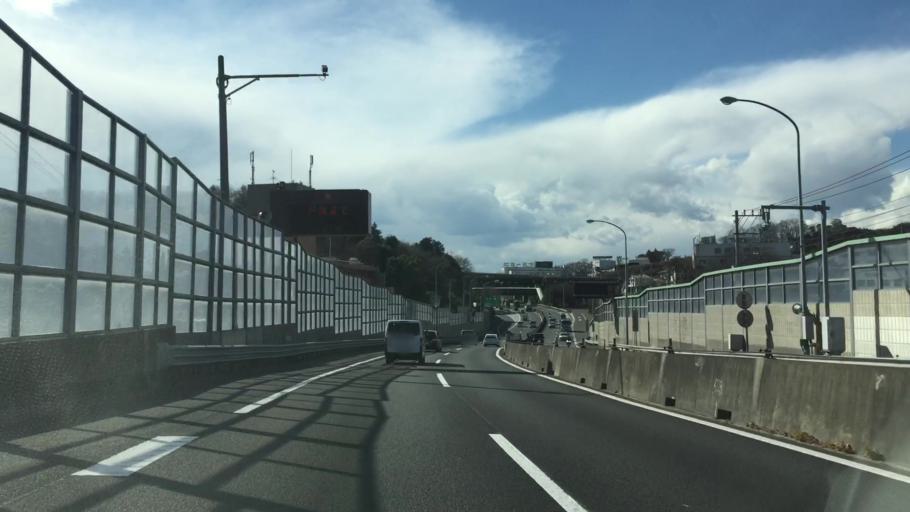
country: JP
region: Kanagawa
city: Yokohama
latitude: 35.4455
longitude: 139.5649
